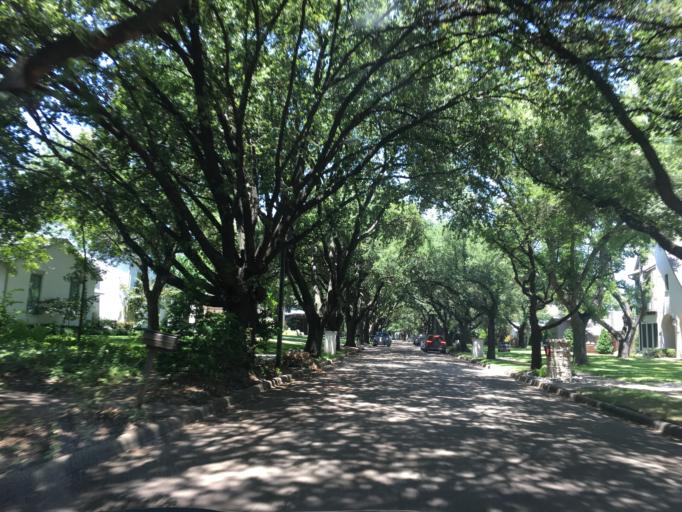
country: US
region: Texas
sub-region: Dallas County
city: Highland Park
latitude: 32.8371
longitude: -96.7353
